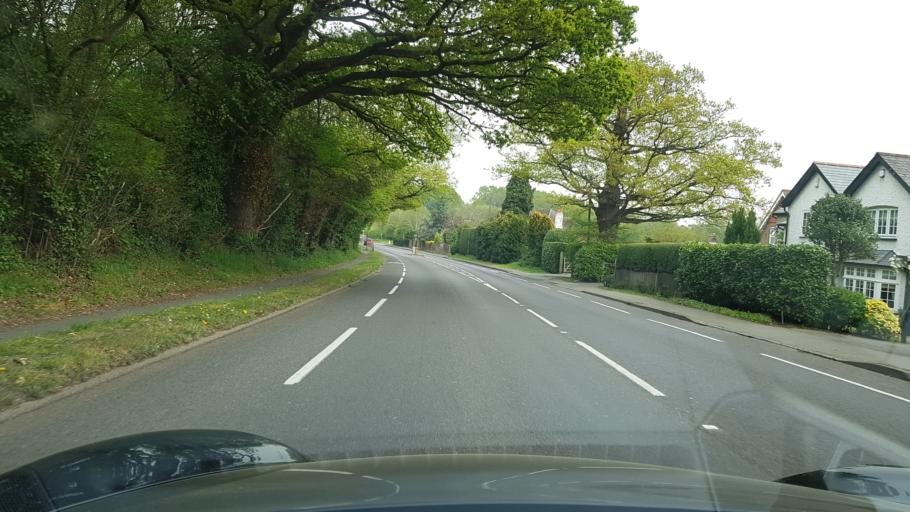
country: GB
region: England
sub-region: Surrey
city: Send
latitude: 51.2832
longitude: -0.5113
